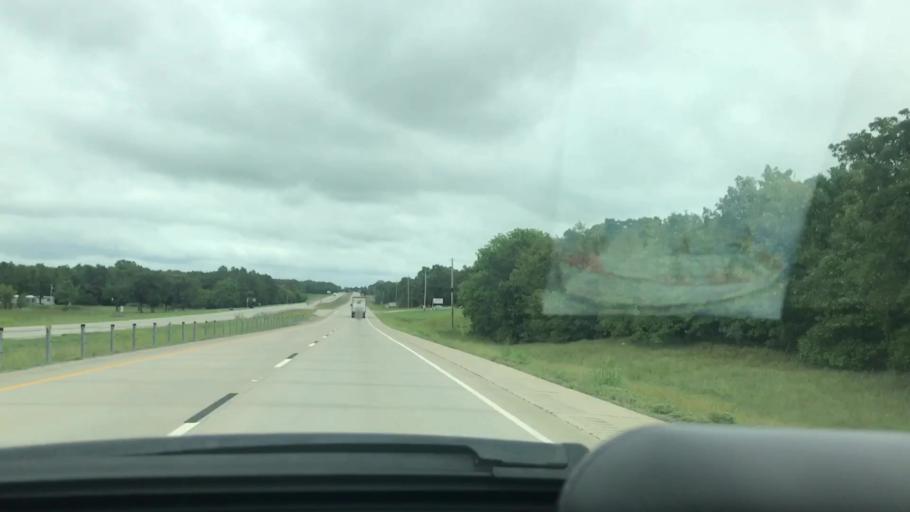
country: US
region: Oklahoma
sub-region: Pittsburg County
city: McAlester
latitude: 34.7011
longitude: -95.9077
